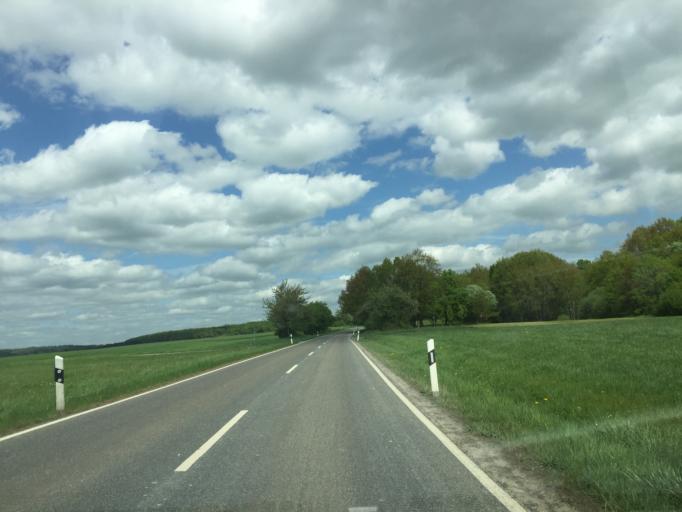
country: DE
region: Rheinland-Pfalz
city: Berod bei Wallmerod
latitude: 50.4756
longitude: 7.9347
